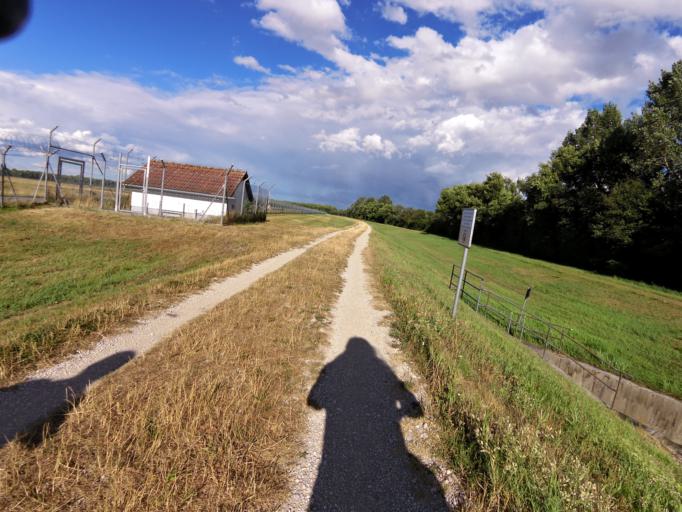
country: DE
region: Bavaria
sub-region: Upper Bavaria
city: Oberding
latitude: 48.3423
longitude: 11.8085
